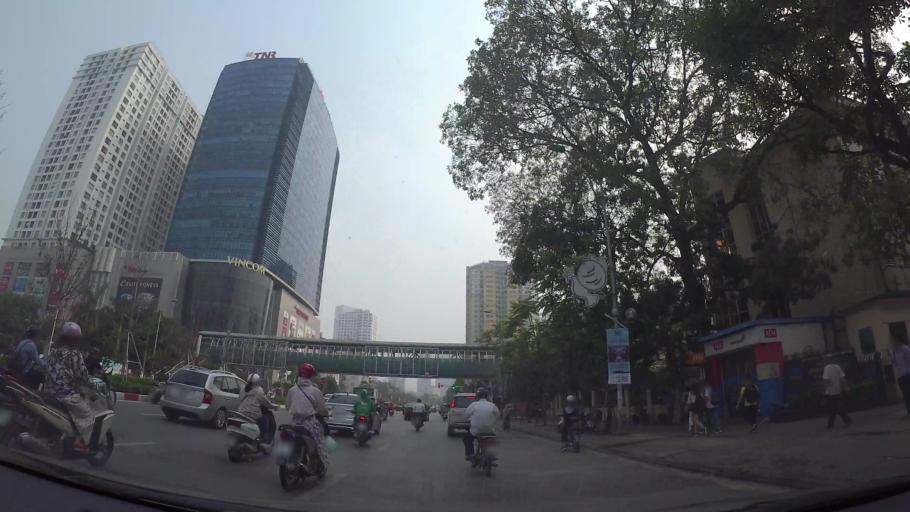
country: VN
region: Ha Noi
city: Cau Giay
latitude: 21.0220
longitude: 105.8096
